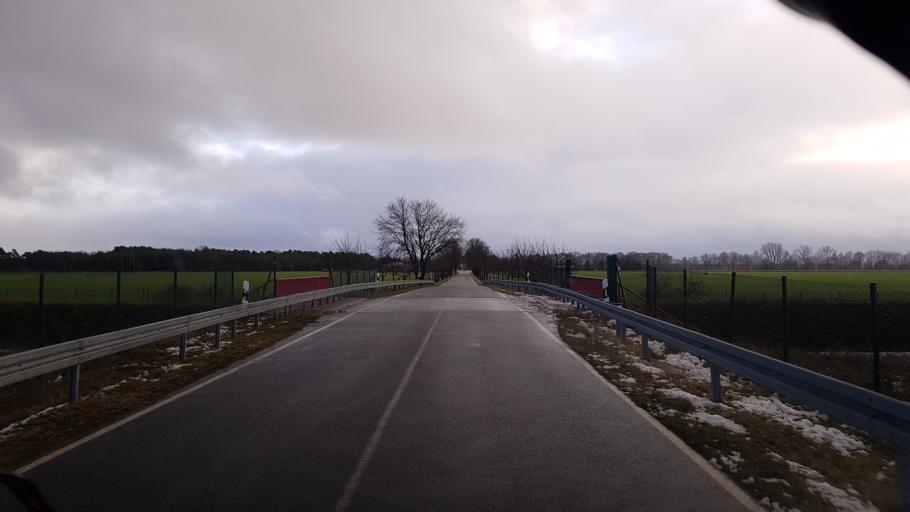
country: DE
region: Brandenburg
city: Heinersbruck
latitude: 51.8296
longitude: 14.5060
